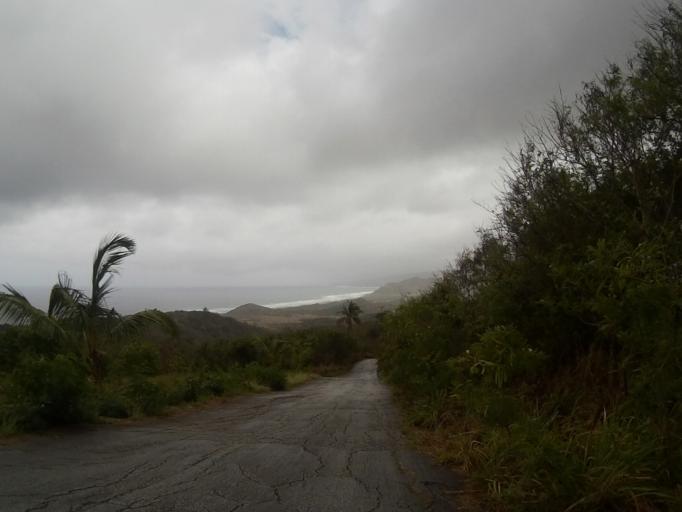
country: BB
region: Saint Andrew
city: Greenland
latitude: 13.2738
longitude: -59.5789
